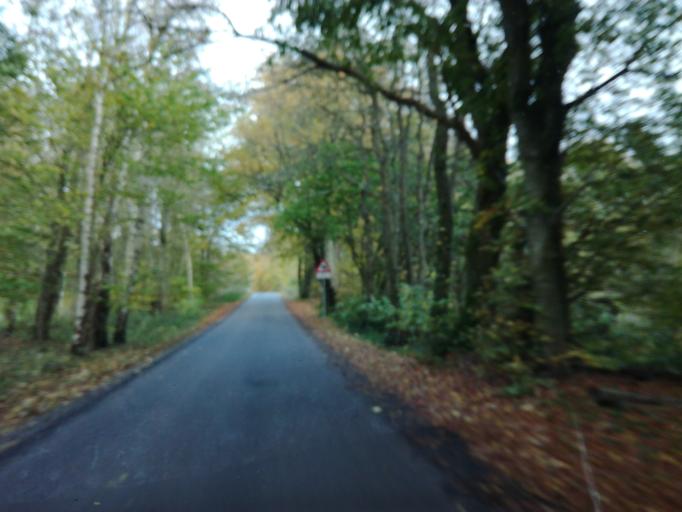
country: DK
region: South Denmark
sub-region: Vejle Kommune
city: Borkop
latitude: 55.6791
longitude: 9.6019
